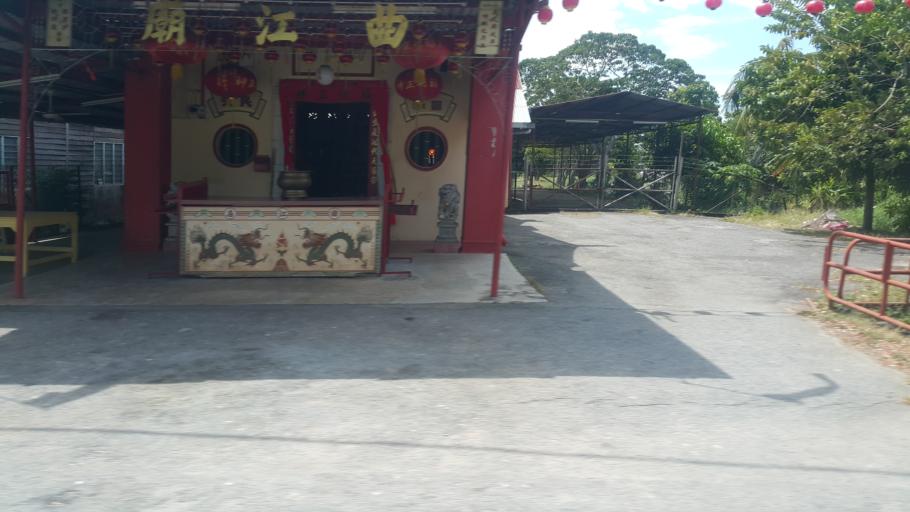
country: MY
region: Melaka
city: Kampung Bukit Baharu
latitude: 2.1865
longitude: 102.2745
